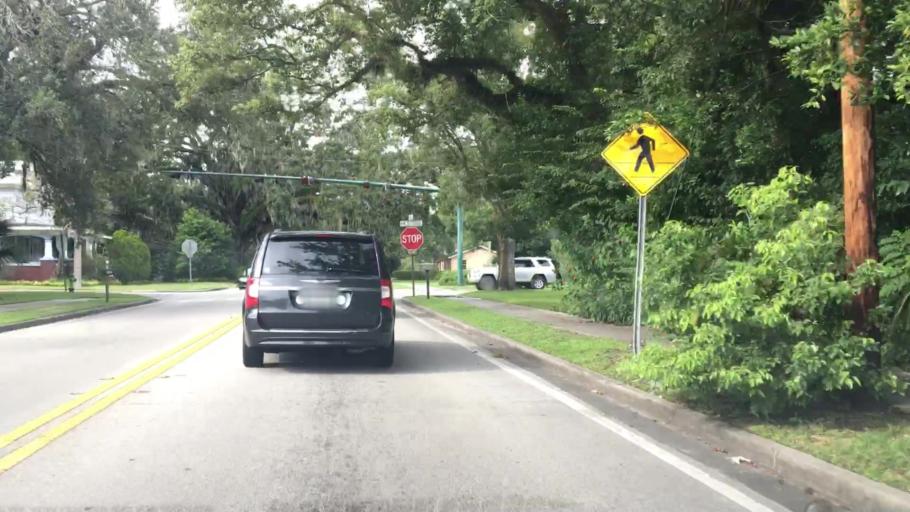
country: US
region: Florida
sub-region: Seminole County
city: Sanford
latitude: 28.7936
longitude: -81.2648
